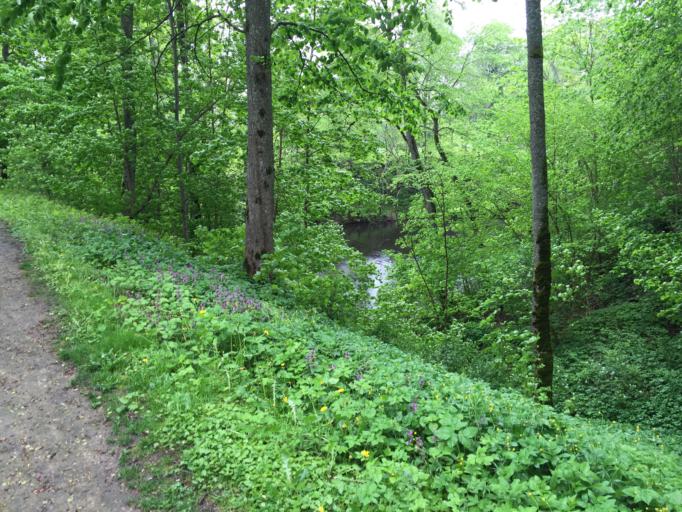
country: LV
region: Lielvarde
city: Lielvarde
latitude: 56.7120
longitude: 24.8380
